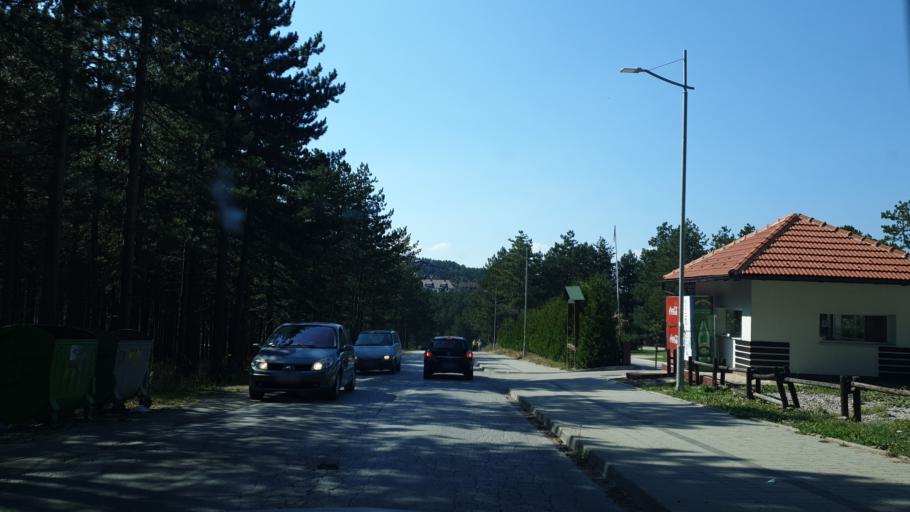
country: RS
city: Zlatibor
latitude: 43.7211
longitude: 19.7089
